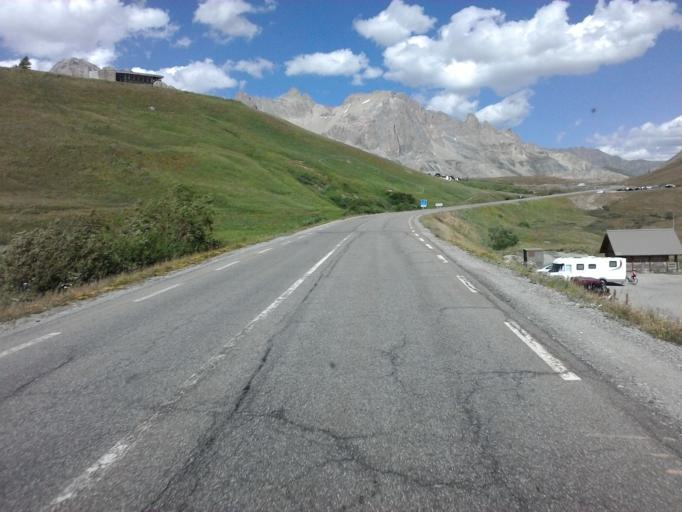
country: FR
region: Provence-Alpes-Cote d'Azur
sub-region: Departement des Hautes-Alpes
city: Le Monetier-les-Bains
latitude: 45.0332
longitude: 6.3982
